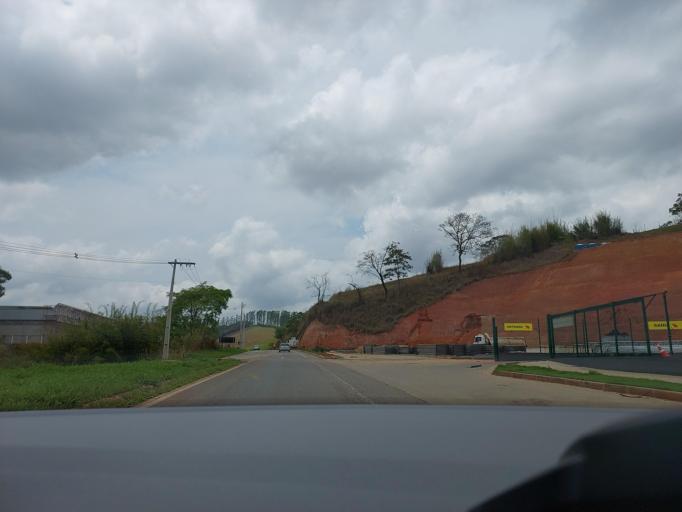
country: BR
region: Minas Gerais
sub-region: Ponte Nova
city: Ponte Nova
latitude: -20.4301
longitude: -42.8928
